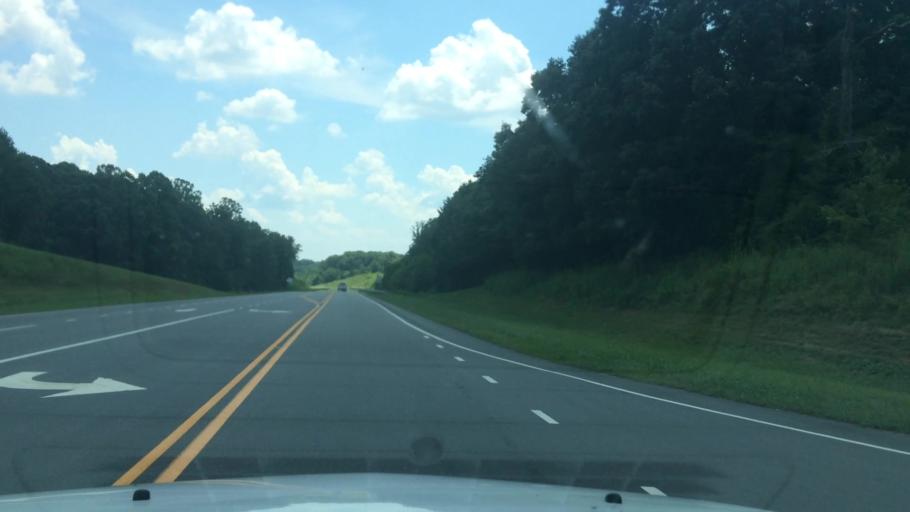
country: US
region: North Carolina
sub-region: Alexander County
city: Stony Point
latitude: 35.8696
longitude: -81.0639
